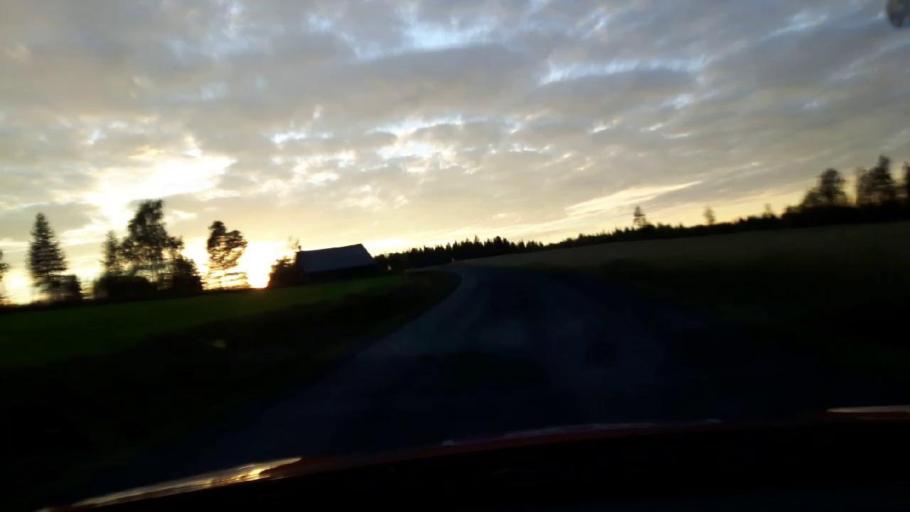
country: SE
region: Jaemtland
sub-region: OEstersunds Kommun
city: Ostersund
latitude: 63.2820
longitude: 14.6957
